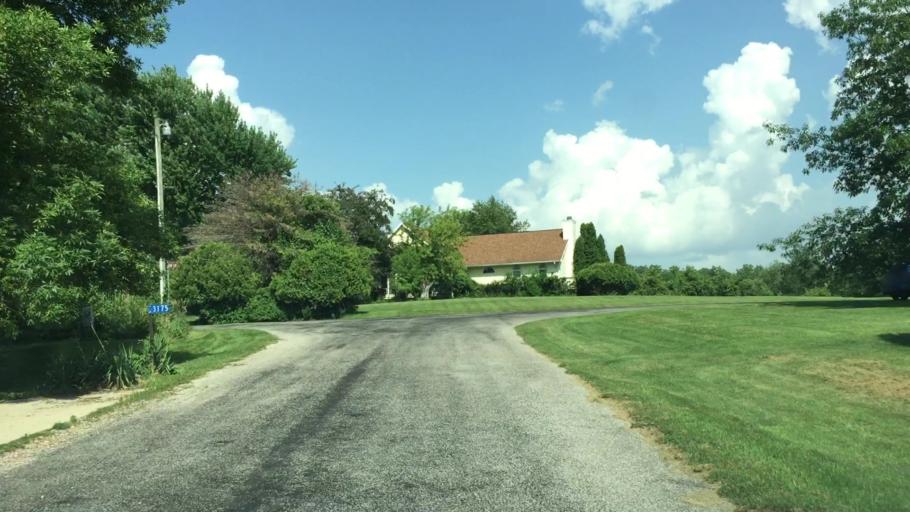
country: US
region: Iowa
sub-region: Johnson County
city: North Liberty
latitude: 41.8052
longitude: -91.6184
